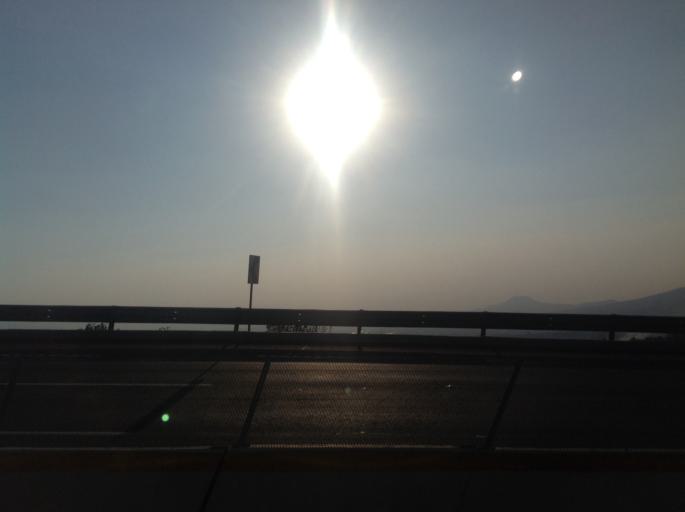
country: MX
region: Mexico
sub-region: Ixtapaluca
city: San Jeronimo Cuatro Vientos
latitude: 19.3042
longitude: -98.7920
